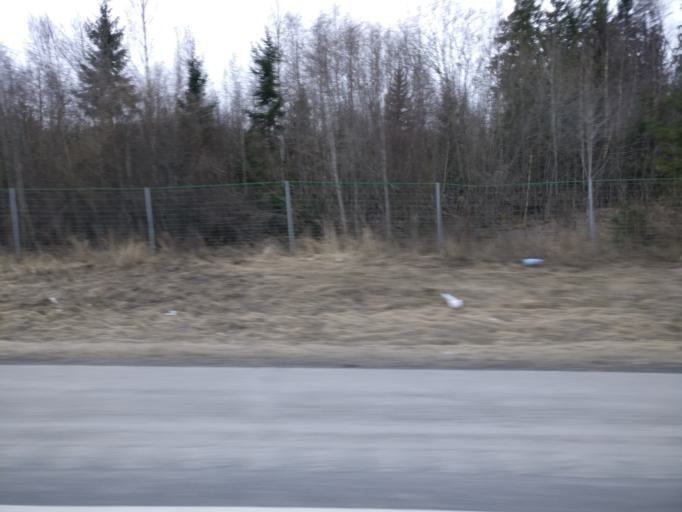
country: FI
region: Pirkanmaa
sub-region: Etelae-Pirkanmaa
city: Akaa
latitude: 61.1727
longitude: 23.9277
